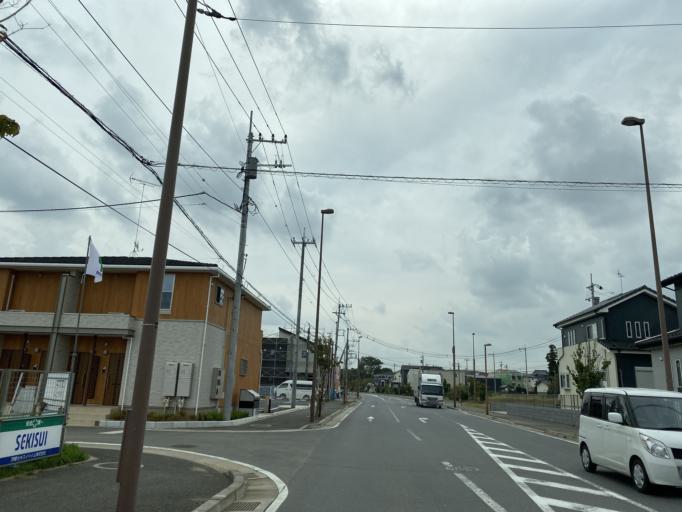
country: JP
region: Ibaraki
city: Mitsukaido
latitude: 36.0184
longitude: 140.0546
